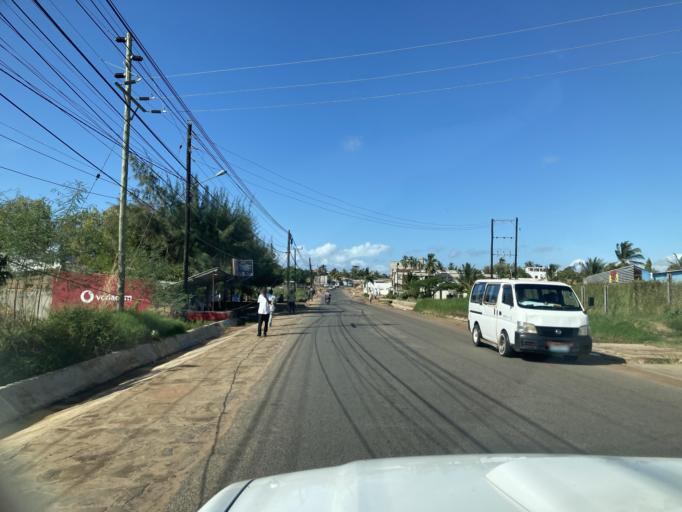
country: MZ
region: Cabo Delgado
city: Pemba
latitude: -12.9748
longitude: 40.5409
